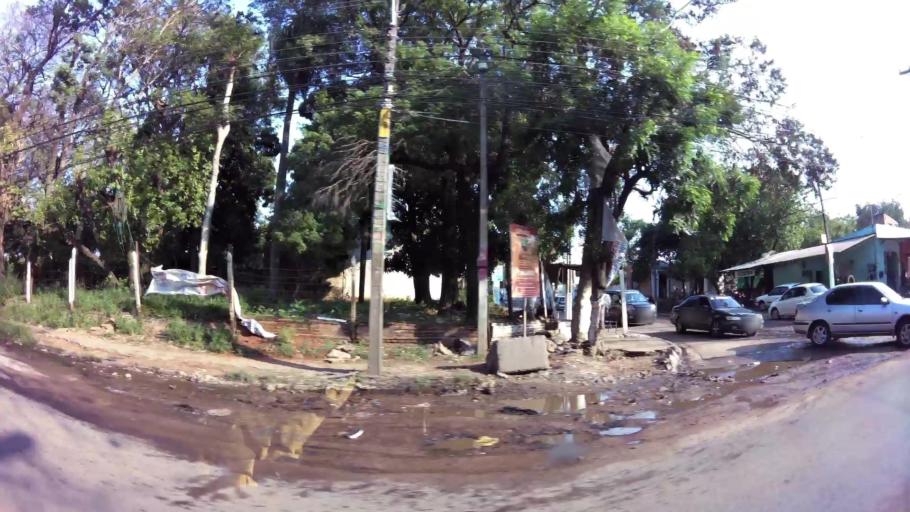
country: PY
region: Central
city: Lambare
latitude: -25.3400
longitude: -57.5936
